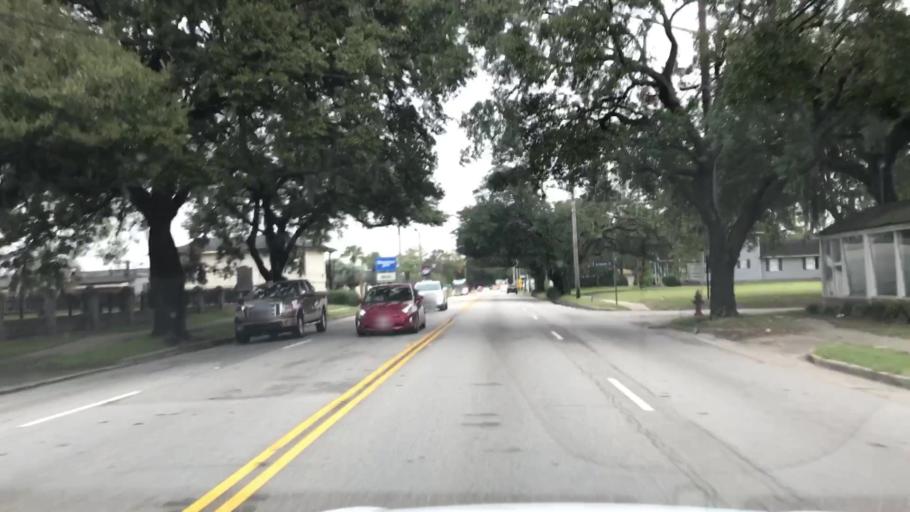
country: US
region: South Carolina
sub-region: Georgetown County
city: Georgetown
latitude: 33.3702
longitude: -79.2782
